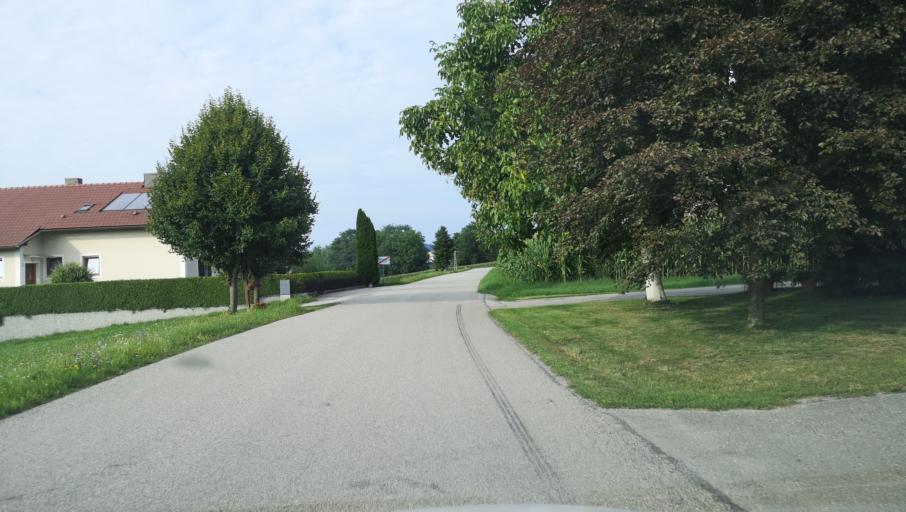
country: AT
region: Lower Austria
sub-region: Politischer Bezirk Amstetten
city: Zeillern
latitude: 48.1668
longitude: 14.8206
